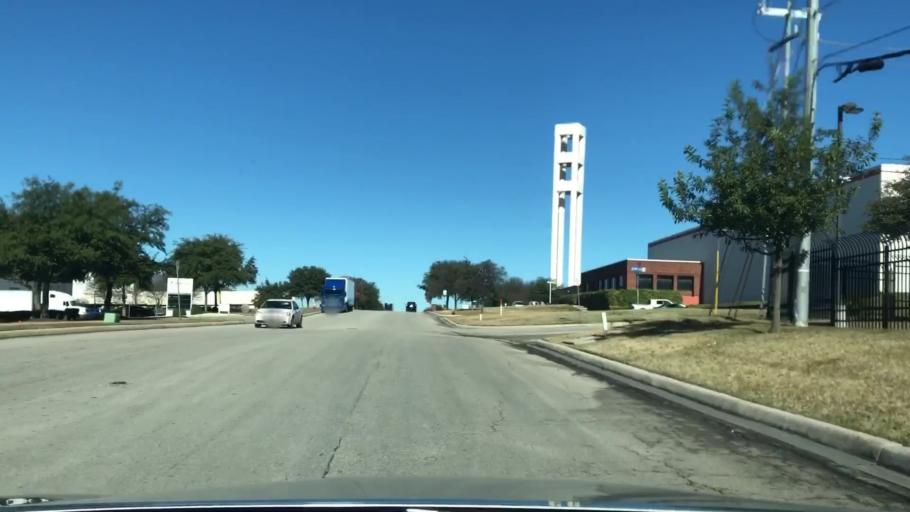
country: US
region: Texas
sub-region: Bexar County
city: Selma
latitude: 29.5990
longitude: -98.2831
